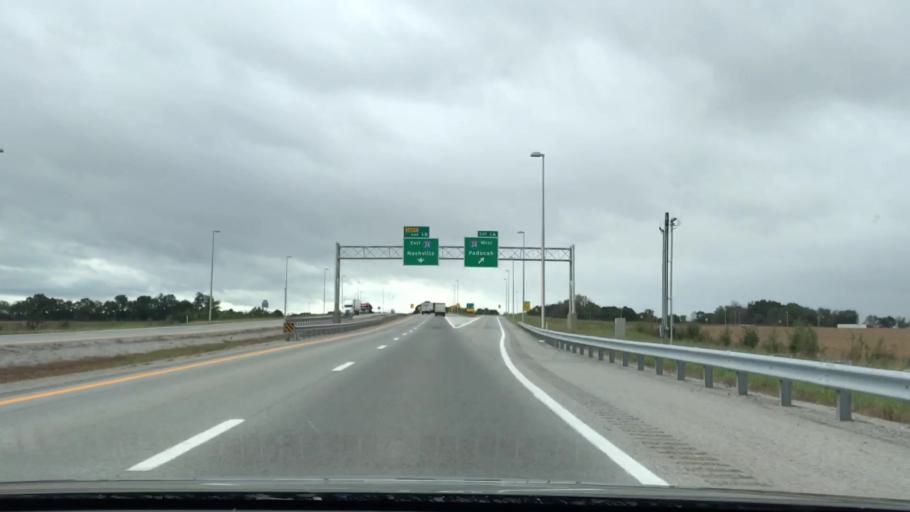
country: US
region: Kentucky
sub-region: Christian County
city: Fort Campbell North
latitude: 36.7497
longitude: -87.5095
